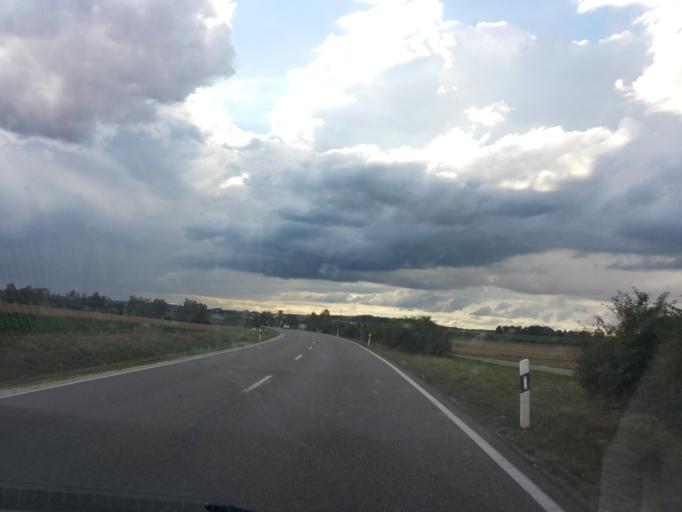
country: DE
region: Bavaria
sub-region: Upper Bavaria
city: Eitensheim
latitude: 48.8289
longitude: 11.3258
